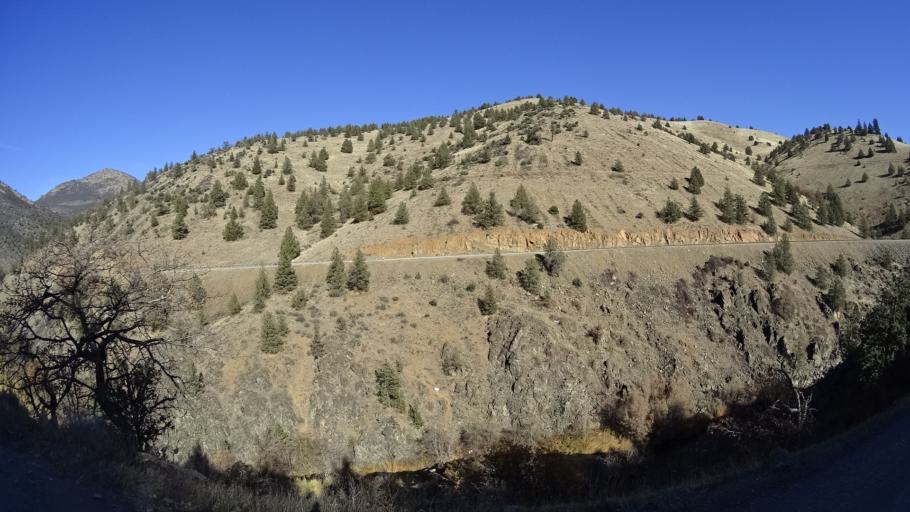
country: US
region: California
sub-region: Siskiyou County
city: Yreka
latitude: 41.7888
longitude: -122.6059
